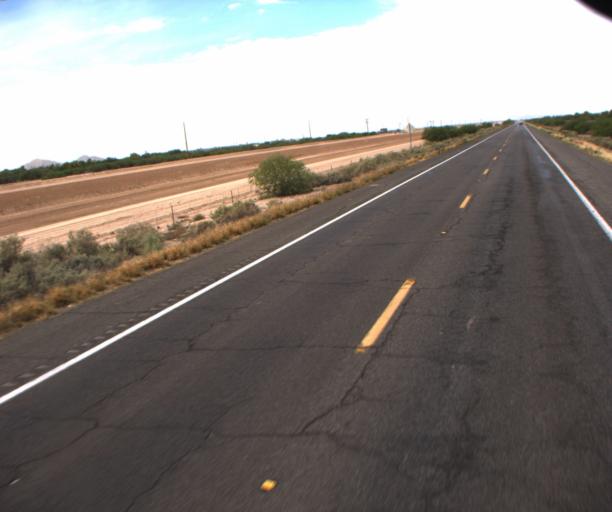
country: US
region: Arizona
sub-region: Pinal County
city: Sacaton
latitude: 33.1536
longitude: -111.7734
